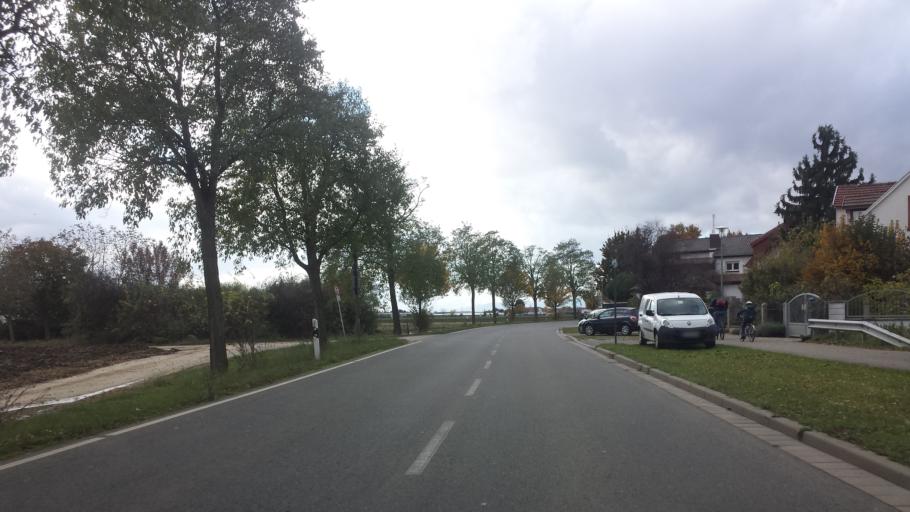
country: DE
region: Rheinland-Pfalz
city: Mutterstadt
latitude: 49.4797
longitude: 8.3501
